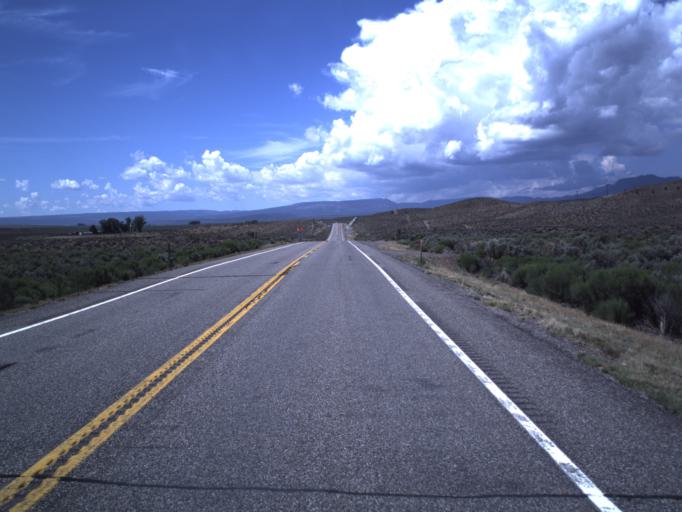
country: US
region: Utah
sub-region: Garfield County
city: Panguitch
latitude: 38.0170
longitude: -112.3688
